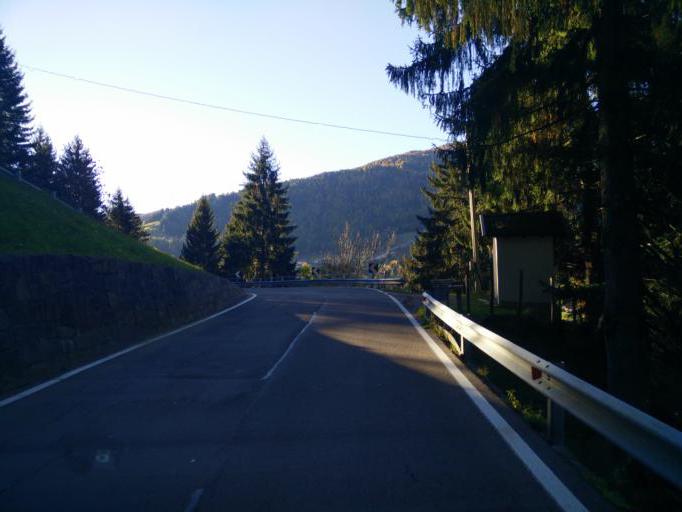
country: IT
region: Trentino-Alto Adige
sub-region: Bolzano
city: Moso in Passiria
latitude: 46.8307
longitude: 11.1710
